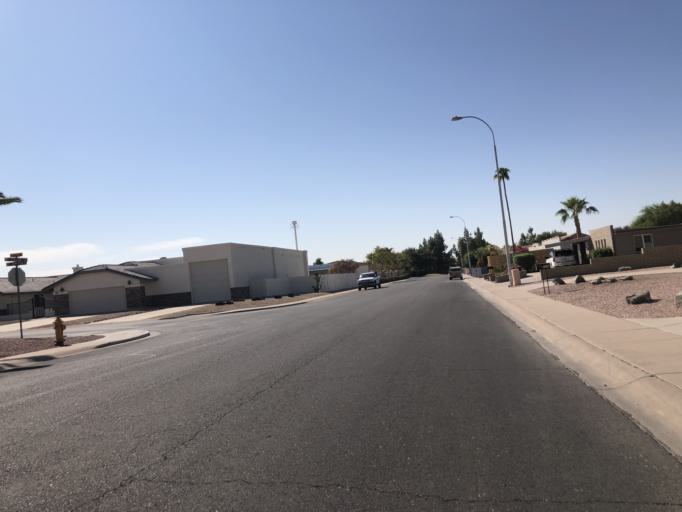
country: US
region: Arizona
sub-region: Maricopa County
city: Chandler
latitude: 33.3001
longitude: -111.9188
